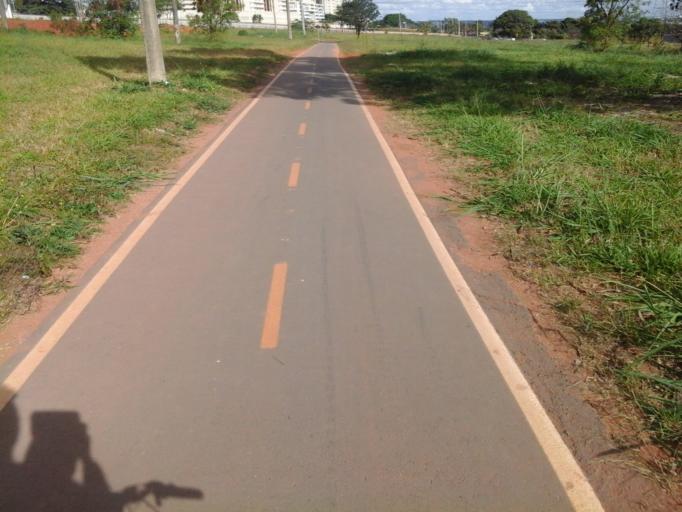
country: BR
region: Federal District
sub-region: Brasilia
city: Brasilia
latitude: -15.8273
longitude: -47.9901
